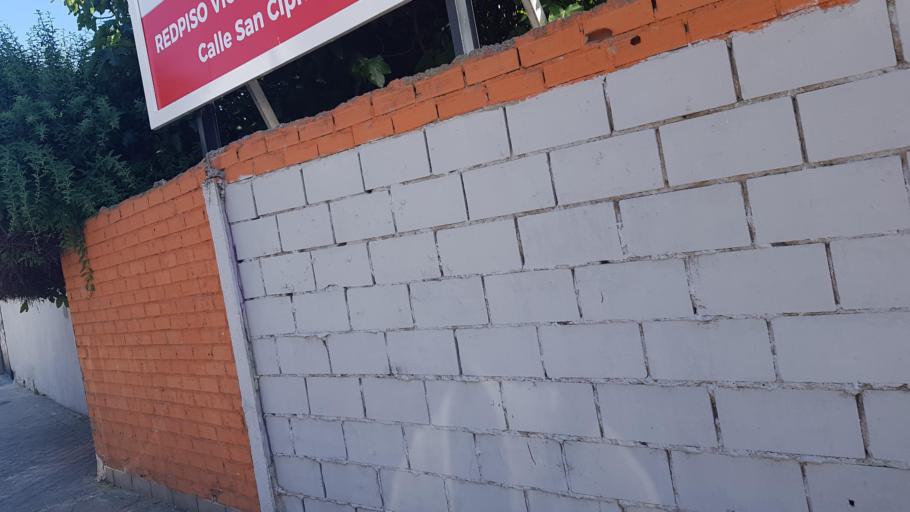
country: ES
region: Madrid
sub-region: Provincia de Madrid
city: Vicalvaro
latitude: 40.4048
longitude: -3.6147
